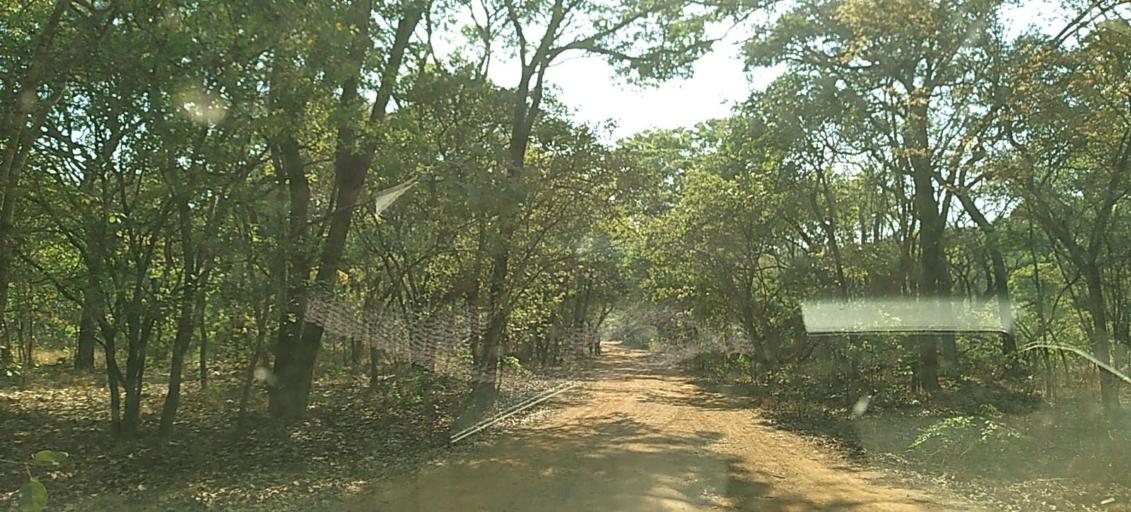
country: ZM
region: Copperbelt
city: Kalulushi
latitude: -13.0052
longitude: 27.7531
